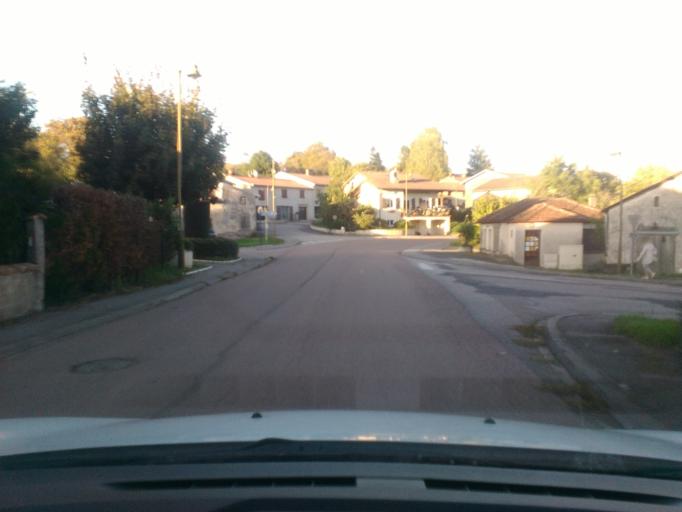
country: FR
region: Lorraine
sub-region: Departement des Vosges
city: Charmes
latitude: 48.3354
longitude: 6.2731
